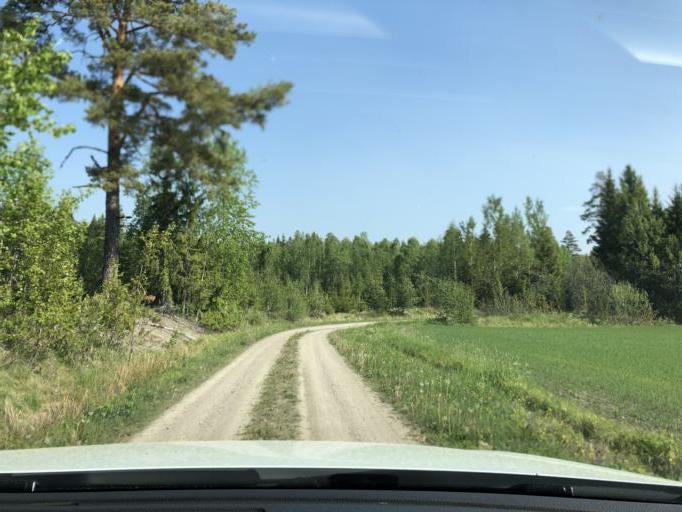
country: SE
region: Dalarna
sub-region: Avesta Kommun
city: Horndal
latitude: 60.2126
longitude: 16.4923
